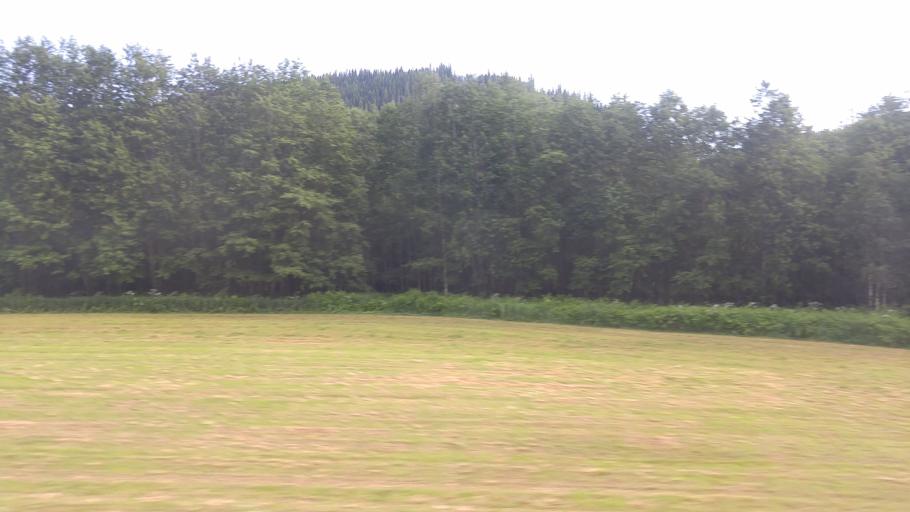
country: NO
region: Nord-Trondelag
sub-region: Levanger
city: Levanger
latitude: 63.4574
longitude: 11.4003
